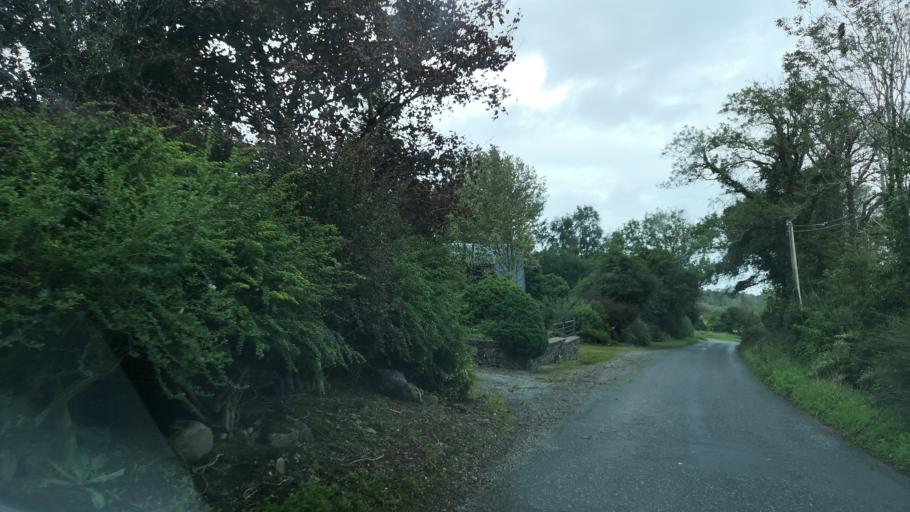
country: IE
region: Connaught
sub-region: County Galway
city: Loughrea
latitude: 53.3043
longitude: -8.6141
